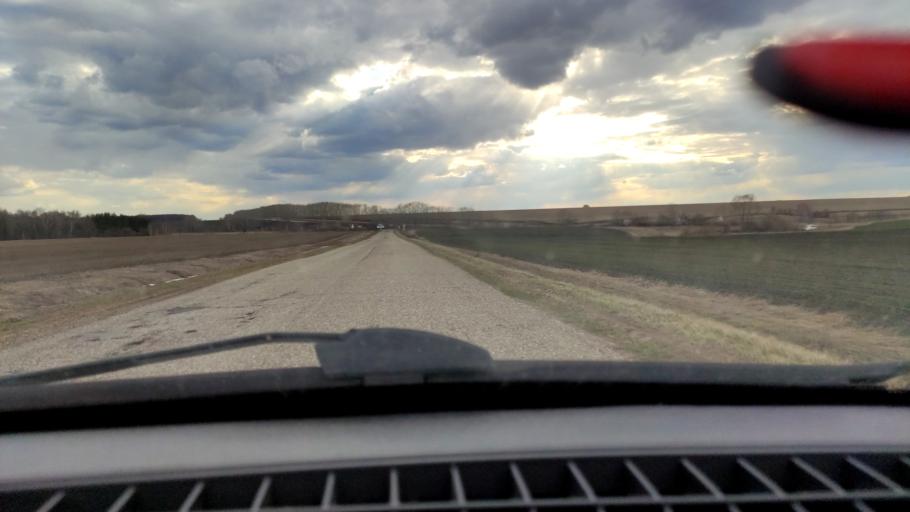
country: RU
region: Bashkortostan
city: Karmaskaly
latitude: 54.3119
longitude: 55.9525
